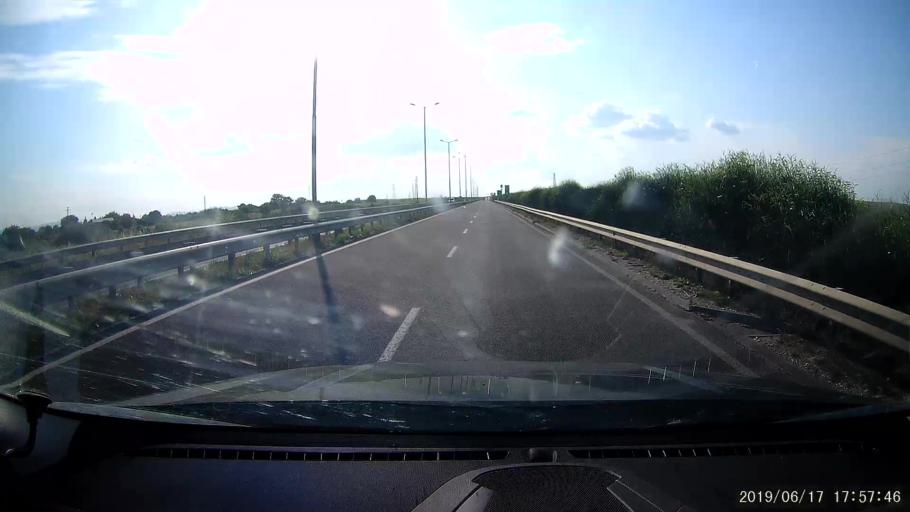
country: BG
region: Khaskovo
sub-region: Obshtina Svilengrad
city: Svilengrad
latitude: 41.7229
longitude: 26.3306
